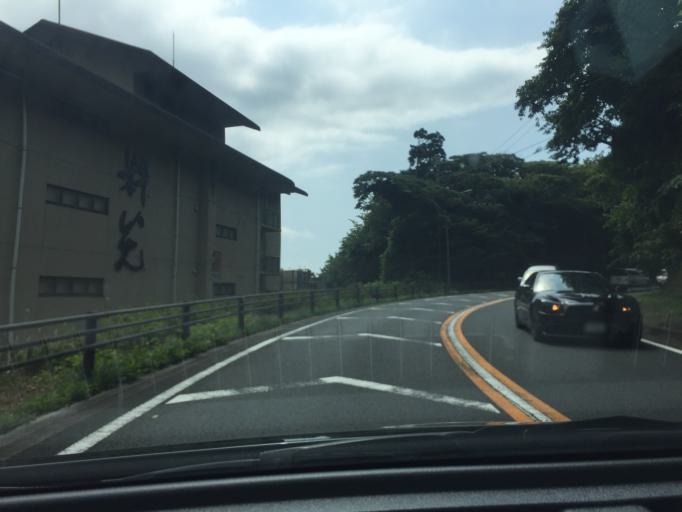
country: JP
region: Shizuoka
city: Ito
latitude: 34.8130
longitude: 139.0695
